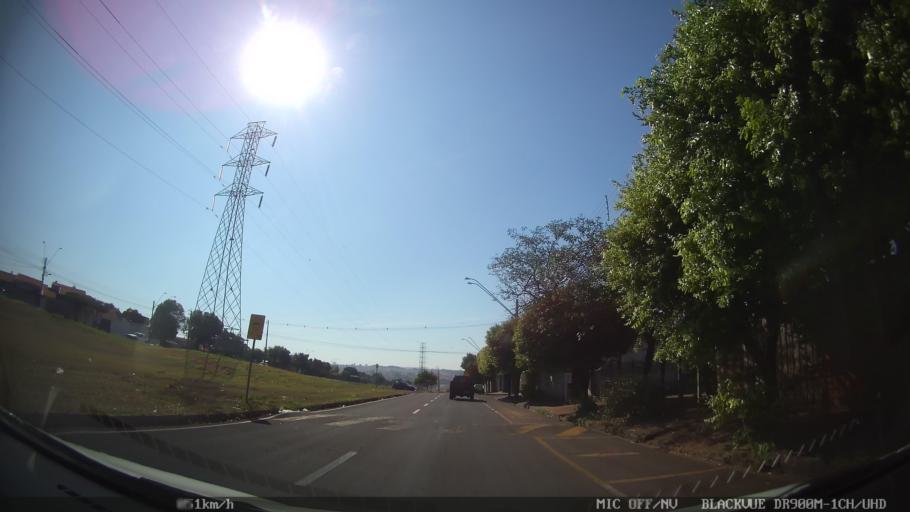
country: BR
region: Sao Paulo
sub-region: Sao Jose Do Rio Preto
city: Sao Jose do Rio Preto
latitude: -20.7656
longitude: -49.3810
